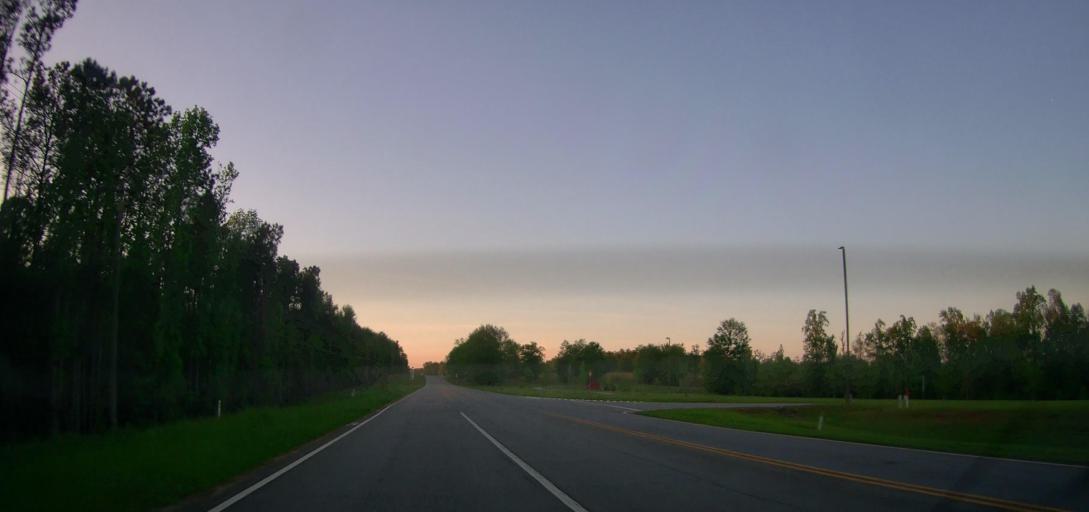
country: US
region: Georgia
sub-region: Marion County
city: Buena Vista
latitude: 32.3633
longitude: -84.5392
